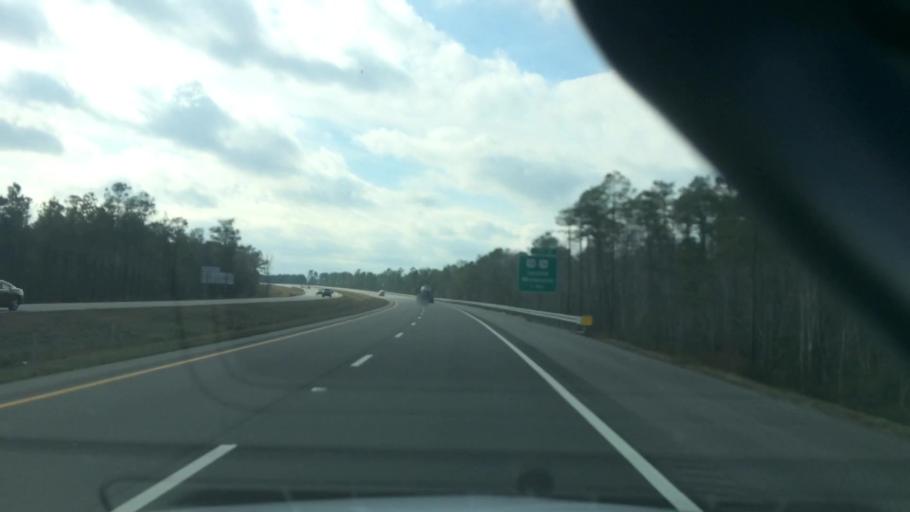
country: US
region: North Carolina
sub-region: Brunswick County
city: Leland
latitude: 34.2775
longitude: -78.0697
